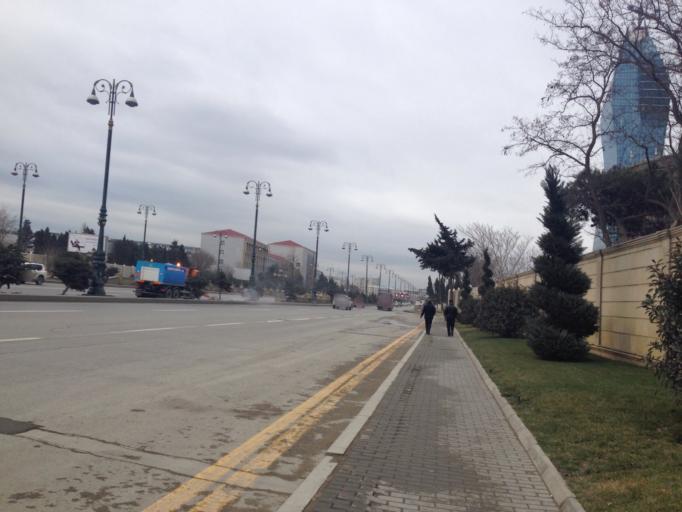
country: AZ
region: Baki
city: Baku
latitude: 40.4071
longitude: 49.8886
